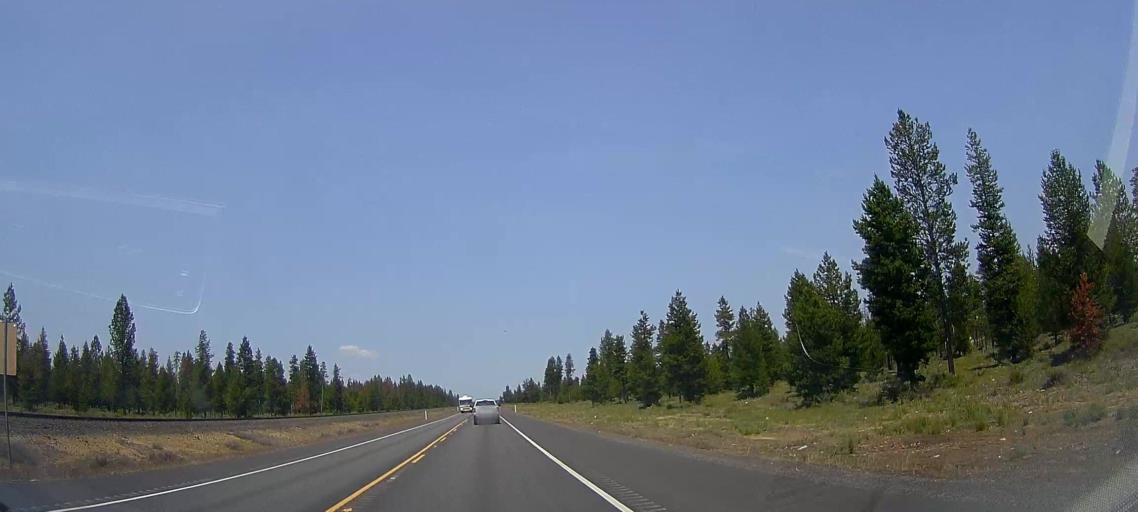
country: US
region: Oregon
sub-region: Deschutes County
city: La Pine
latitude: 43.7293
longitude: -121.4699
